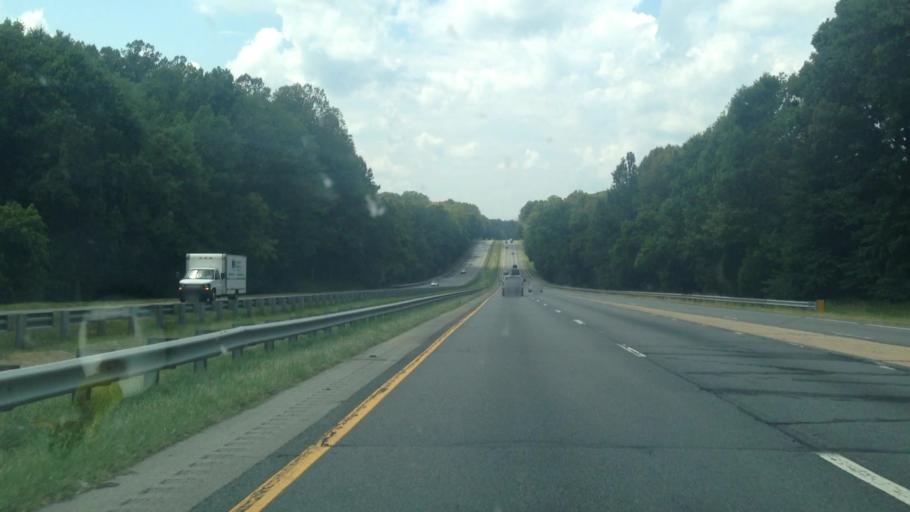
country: US
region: North Carolina
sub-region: Forsyth County
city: Rural Hall
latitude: 36.2307
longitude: -80.3277
